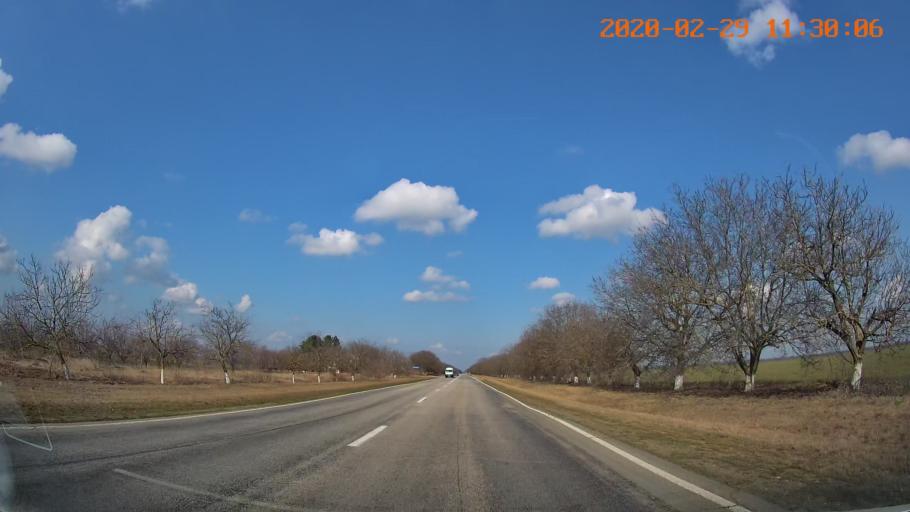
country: MD
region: Telenesti
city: Cocieri
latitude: 47.5045
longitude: 29.1188
